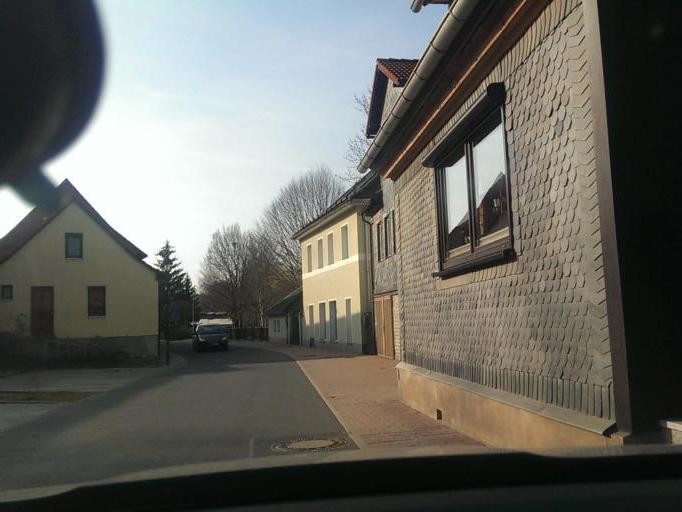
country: DE
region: Thuringia
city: Suhl
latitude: 50.6007
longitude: 10.6888
